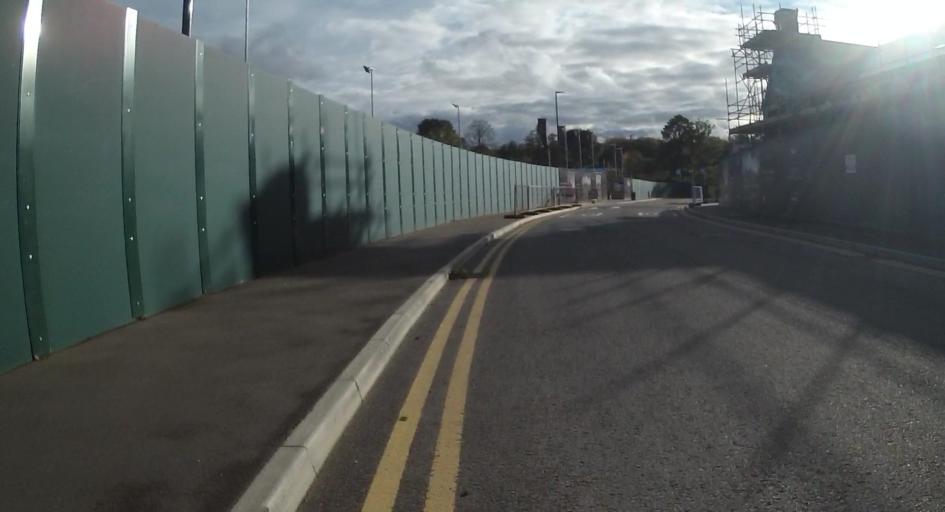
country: GB
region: England
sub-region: Surrey
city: Frimley
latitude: 51.3055
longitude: -0.7032
